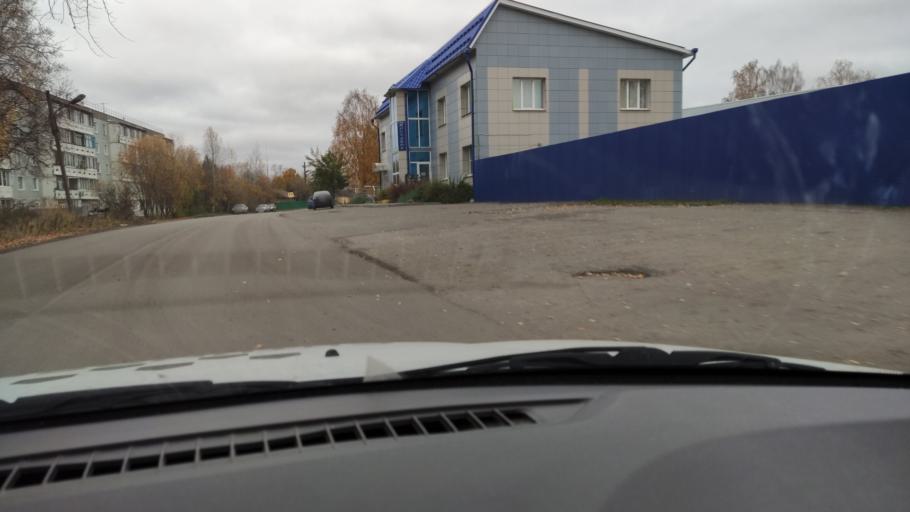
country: RU
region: Kirov
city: Slobodskoy
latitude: 58.7201
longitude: 50.1751
